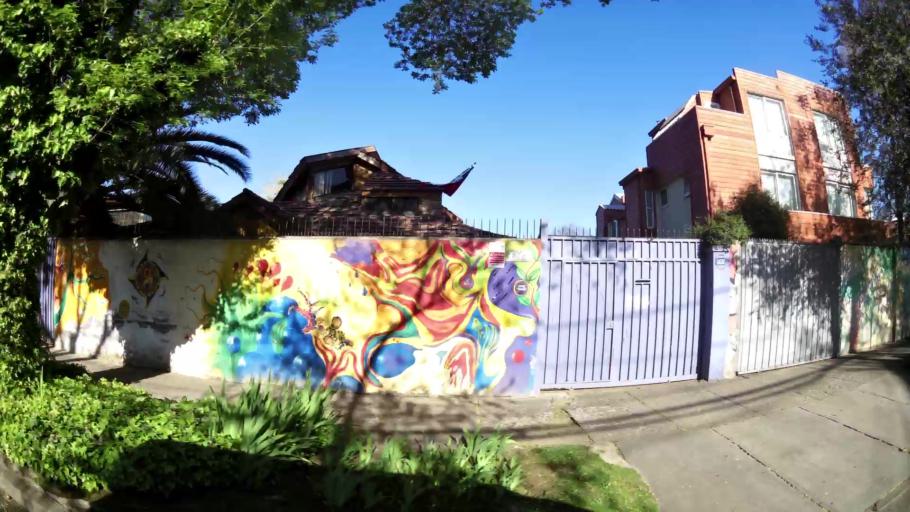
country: CL
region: Santiago Metropolitan
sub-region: Provincia de Santiago
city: Villa Presidente Frei, Nunoa, Santiago, Chile
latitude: -33.4495
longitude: -70.5676
